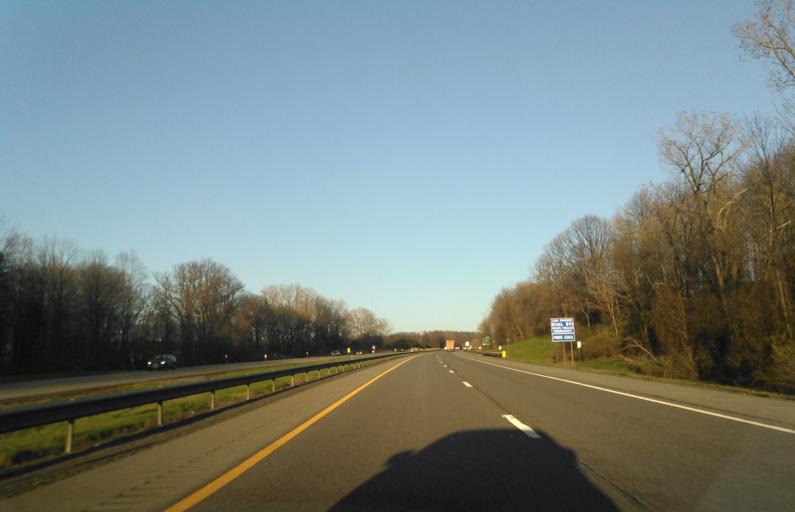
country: US
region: New York
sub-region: Ontario County
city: Victor
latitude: 43.0141
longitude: -77.4636
